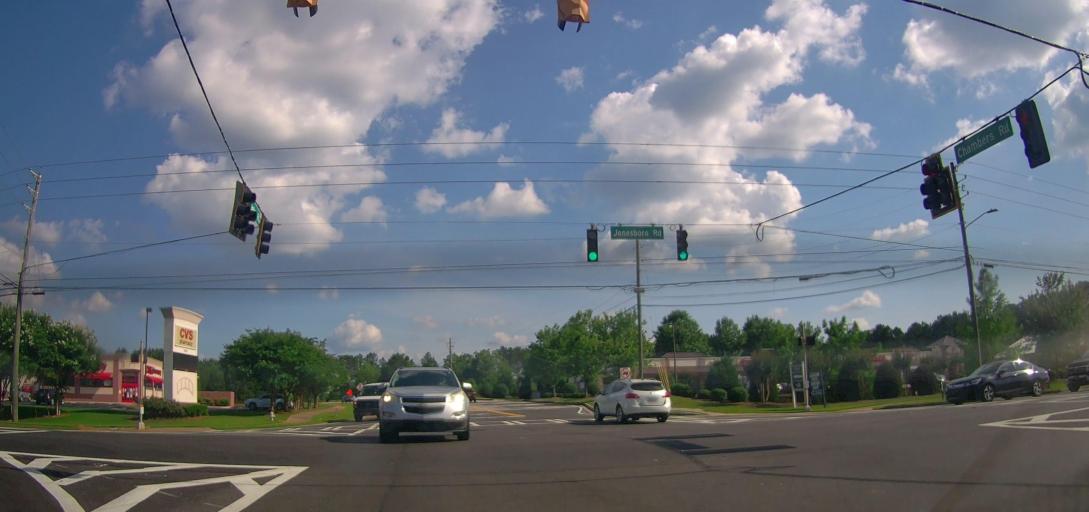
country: US
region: Georgia
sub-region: Henry County
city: Stockbridge
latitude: 33.4646
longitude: -84.2323
